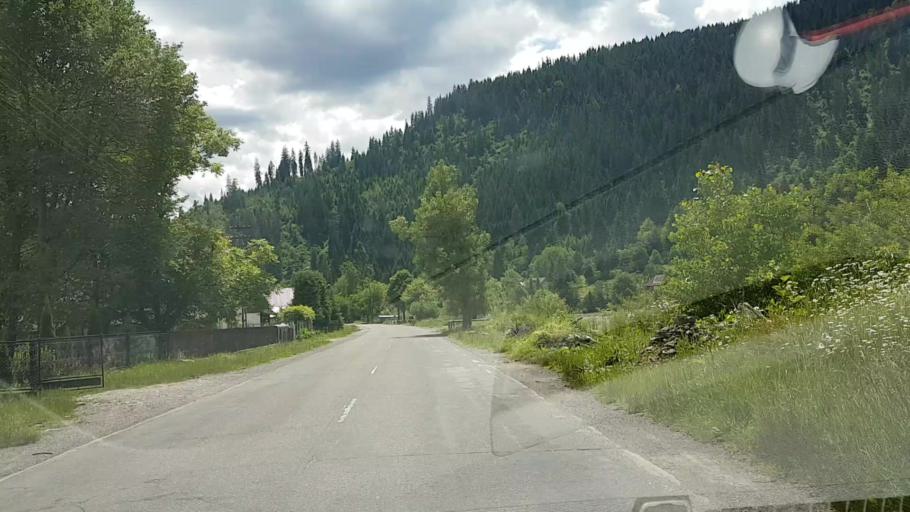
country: RO
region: Suceava
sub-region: Comuna Brosteni
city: Brosteni
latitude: 47.2431
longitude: 25.6911
